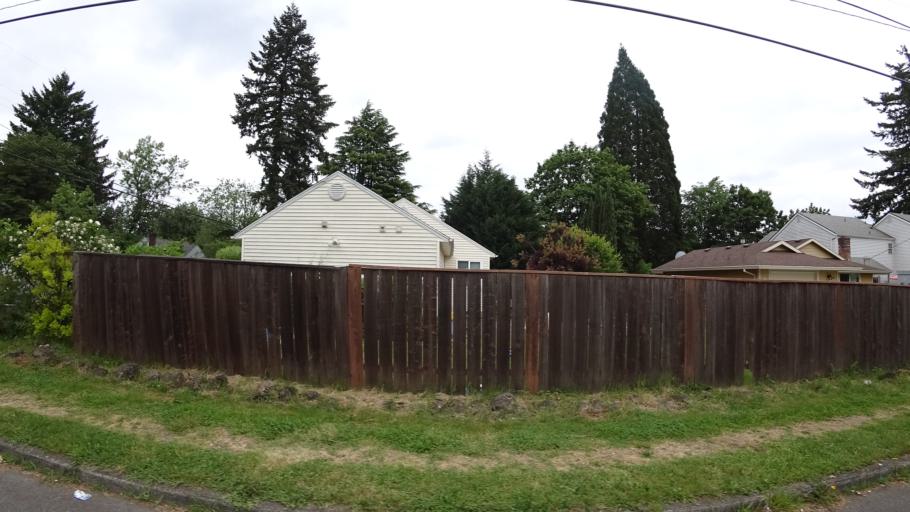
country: US
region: Oregon
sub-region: Multnomah County
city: Lents
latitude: 45.5058
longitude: -122.5356
